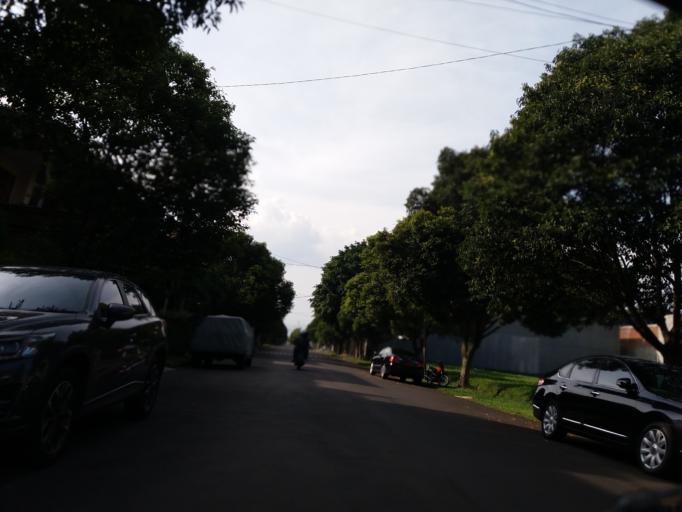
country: ID
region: West Java
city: Bandung
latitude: -6.9612
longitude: 107.6300
